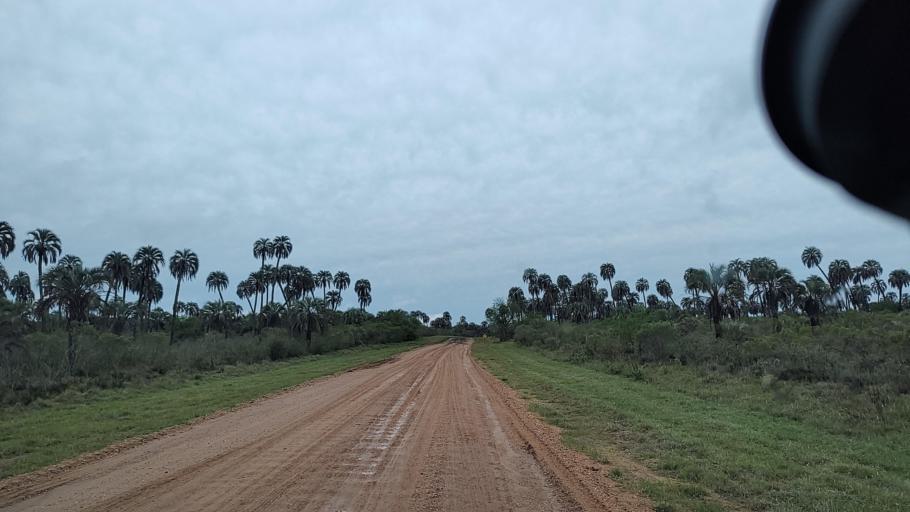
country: AR
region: Entre Rios
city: Ubajay
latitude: -31.8501
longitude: -58.3056
